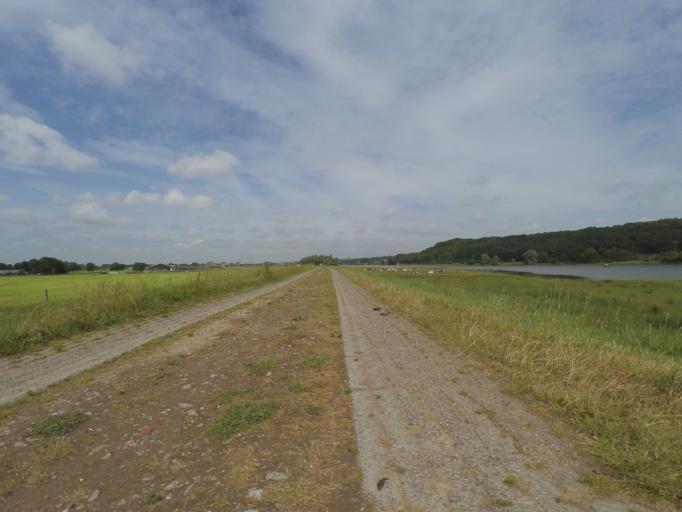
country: NL
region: Utrecht
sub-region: Gemeente Rhenen
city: Rhenen
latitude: 51.9468
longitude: 5.5938
